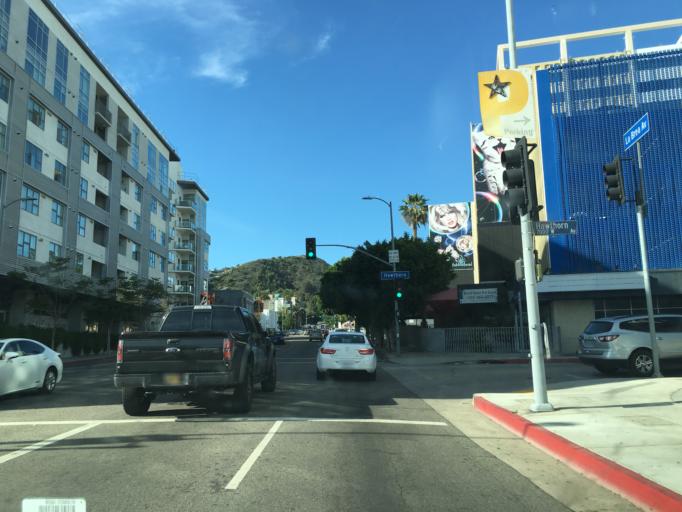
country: US
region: California
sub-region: Los Angeles County
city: Hollywood
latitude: 34.1001
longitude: -118.3447
